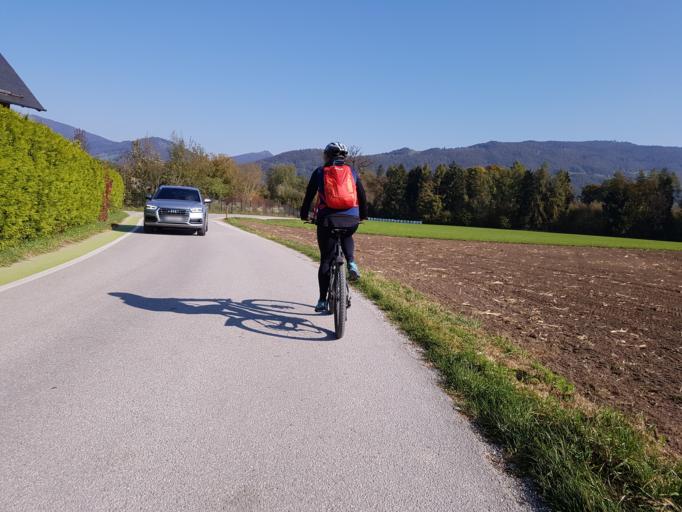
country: AT
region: Salzburg
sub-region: Politischer Bezirk Salzburg-Umgebung
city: Anif
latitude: 47.7428
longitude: 13.0648
